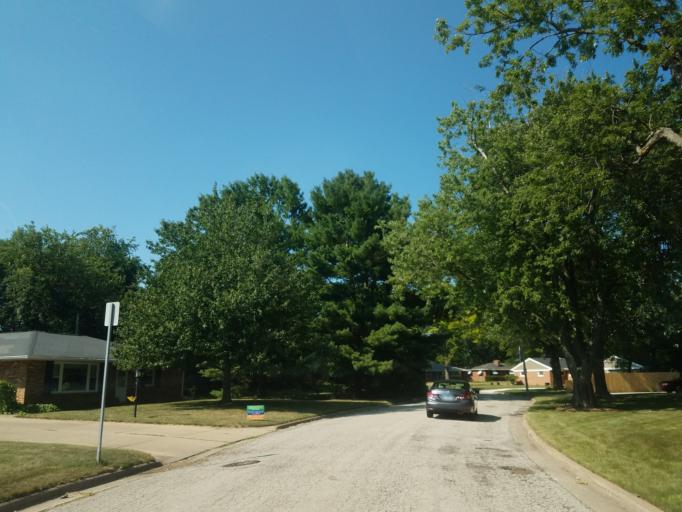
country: US
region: Illinois
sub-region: McLean County
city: Bloomington
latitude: 40.4745
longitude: -88.9595
